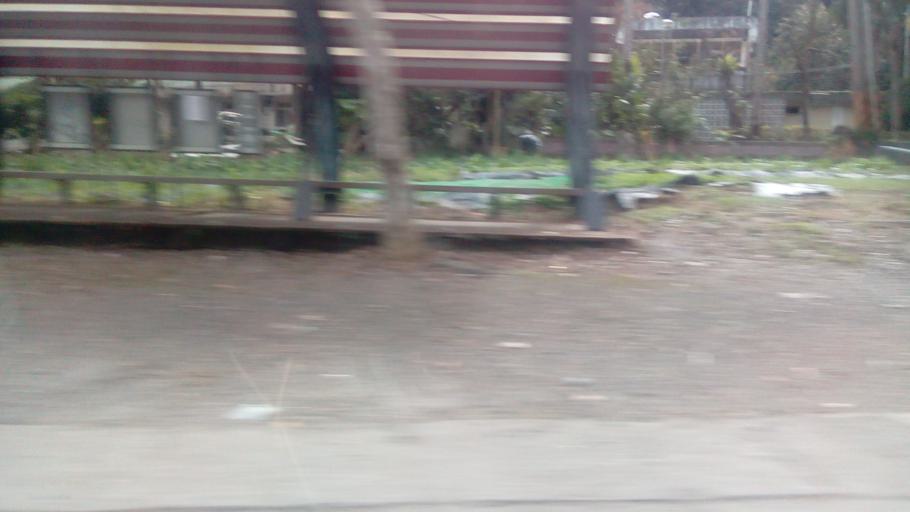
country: TW
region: Taiwan
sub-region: Yilan
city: Yilan
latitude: 24.5756
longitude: 121.4779
